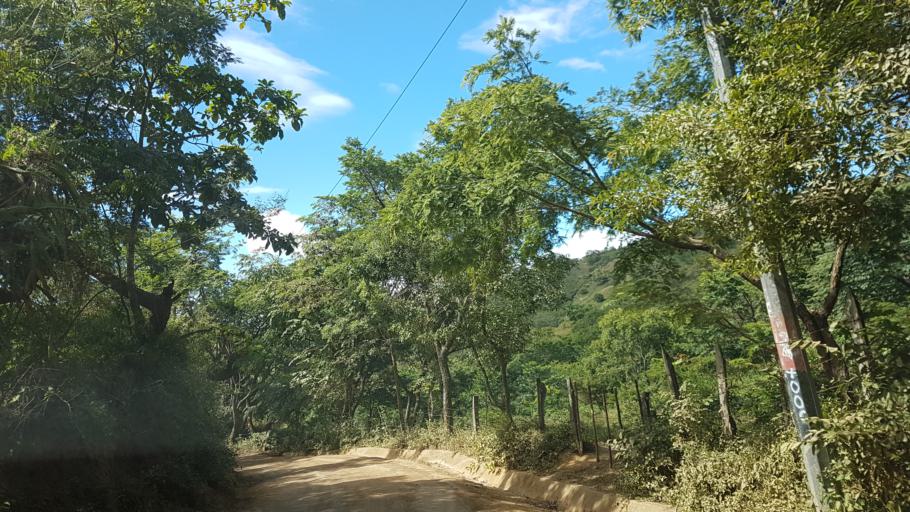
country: HN
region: El Paraiso
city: Santa Cruz
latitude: 13.7394
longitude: -86.6710
